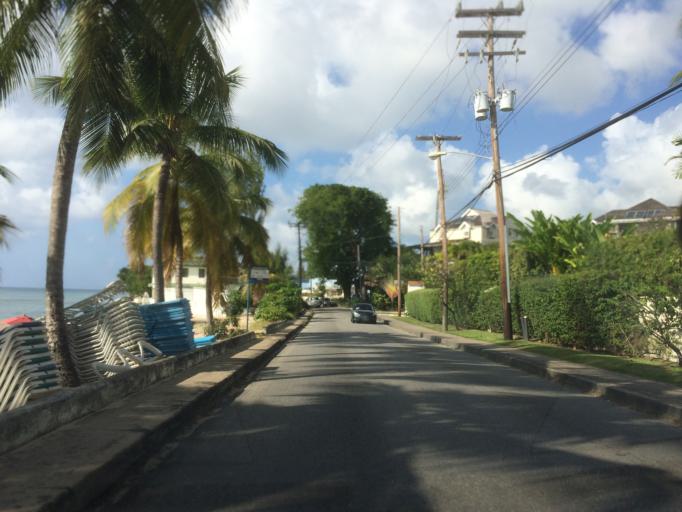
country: BB
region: Saint Peter
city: Speightstown
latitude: 13.2344
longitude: -59.6423
